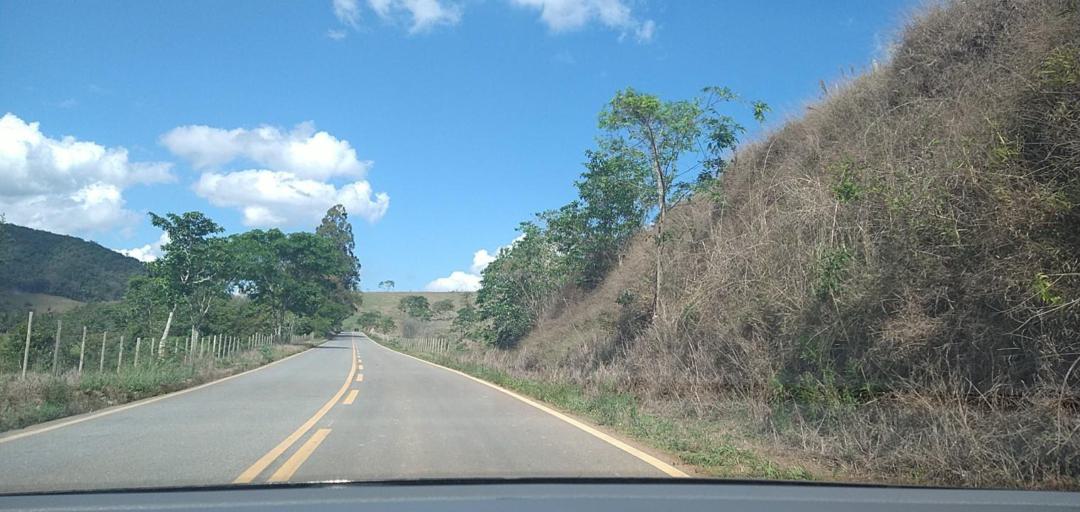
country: BR
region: Minas Gerais
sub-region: Alvinopolis
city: Alvinopolis
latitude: -20.0171
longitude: -43.0925
